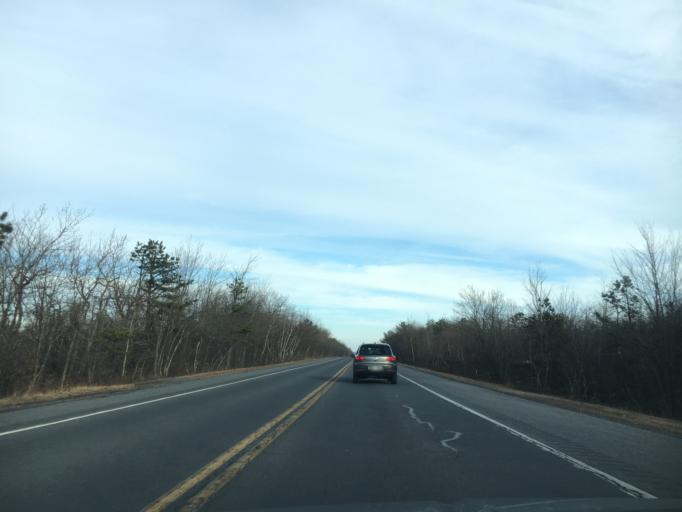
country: US
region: Pennsylvania
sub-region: Luzerne County
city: Hazleton
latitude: 40.9353
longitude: -75.9633
